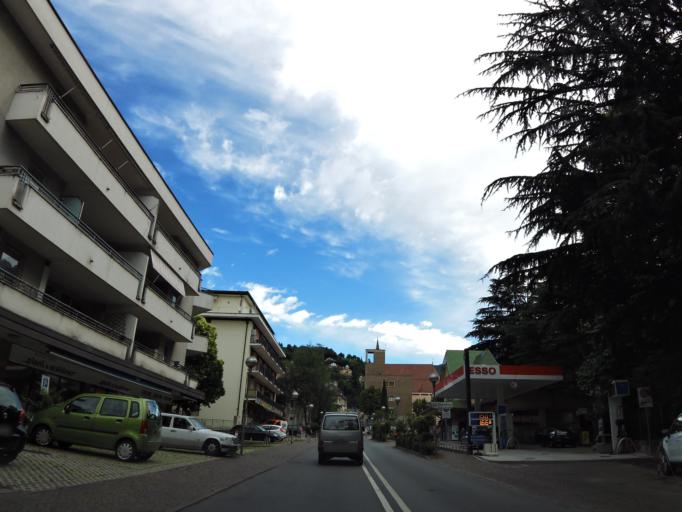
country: IT
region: Trentino-Alto Adige
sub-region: Bolzano
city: Merano
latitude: 46.6672
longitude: 11.1623
